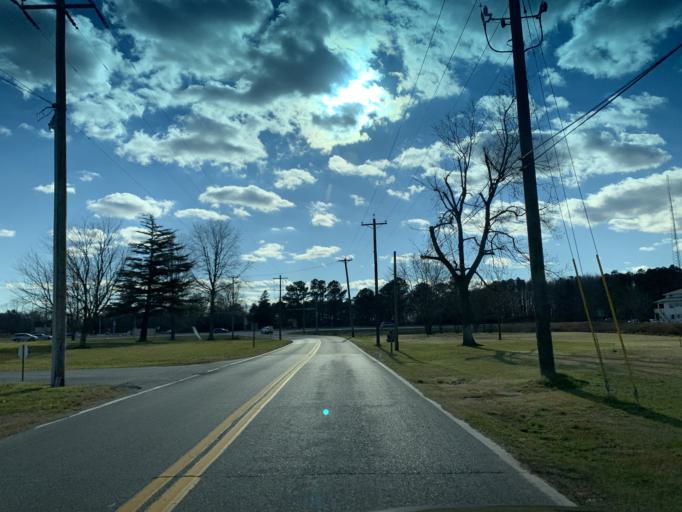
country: US
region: Maryland
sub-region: Worcester County
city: Berlin
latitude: 38.3449
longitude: -75.2193
